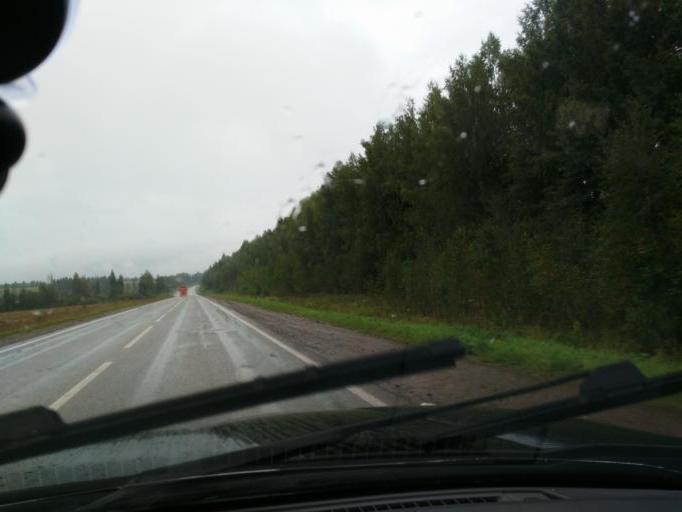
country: RU
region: Perm
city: Osa
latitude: 57.3802
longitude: 55.6093
